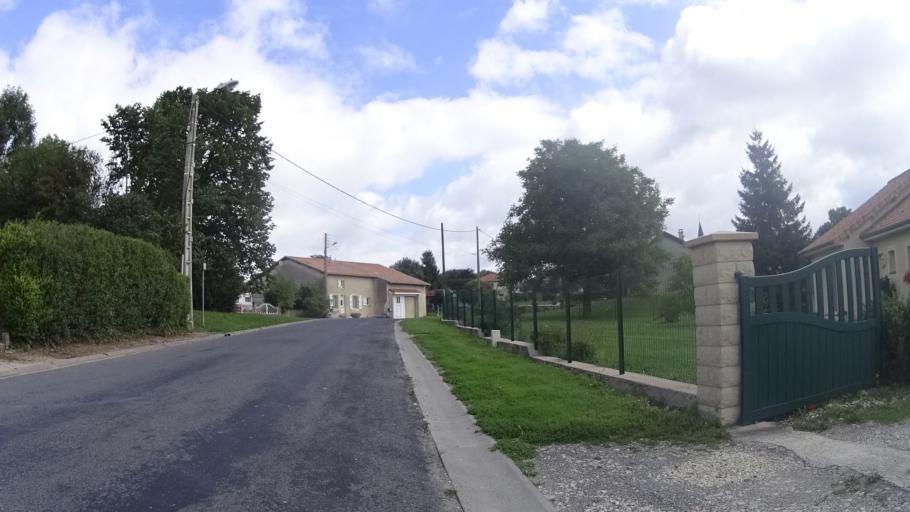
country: FR
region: Lorraine
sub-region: Departement de la Meuse
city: Ligny-en-Barrois
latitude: 48.7416
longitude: 5.3891
